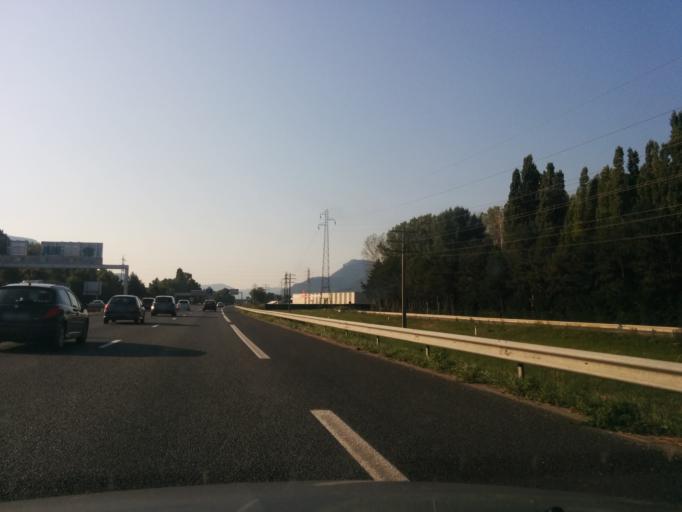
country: FR
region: Rhone-Alpes
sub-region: Departement de l'Isere
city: Saint-Egreve
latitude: 45.2299
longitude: 5.6662
